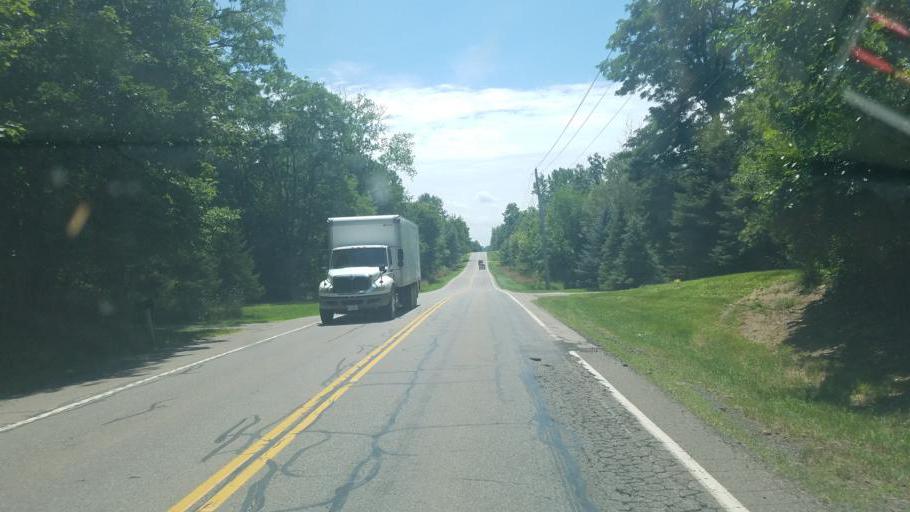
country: US
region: Ohio
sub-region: Richland County
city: Lincoln Heights
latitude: 40.8767
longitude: -82.5135
